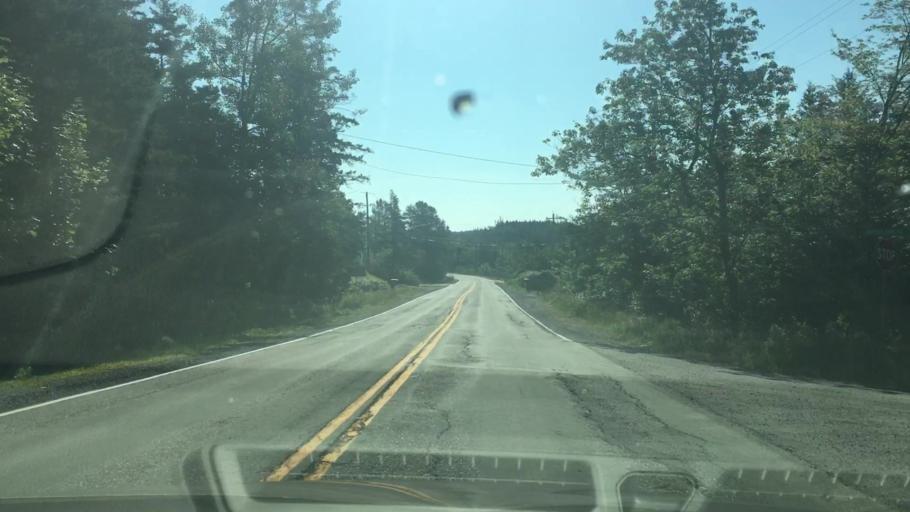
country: CA
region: Nova Scotia
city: Cole Harbour
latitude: 44.7769
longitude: -63.0571
